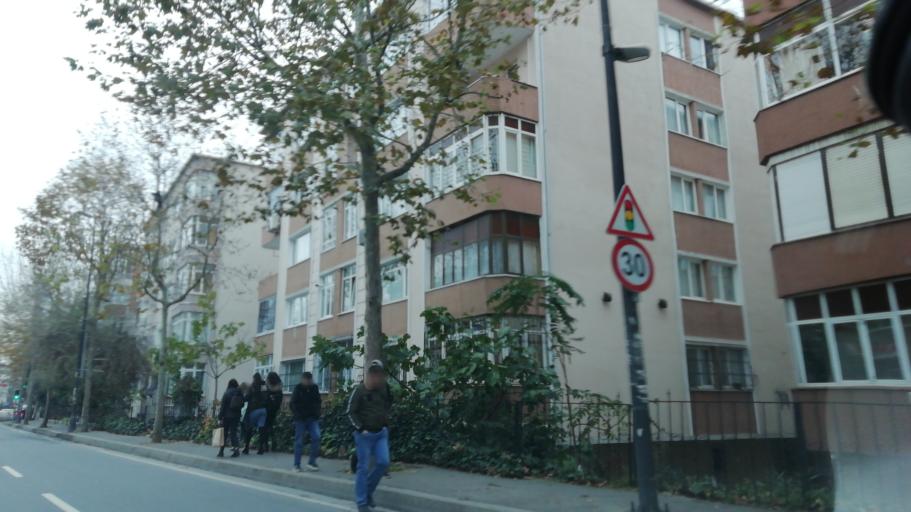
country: TR
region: Istanbul
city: Mahmutbey
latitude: 41.0193
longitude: 28.8267
